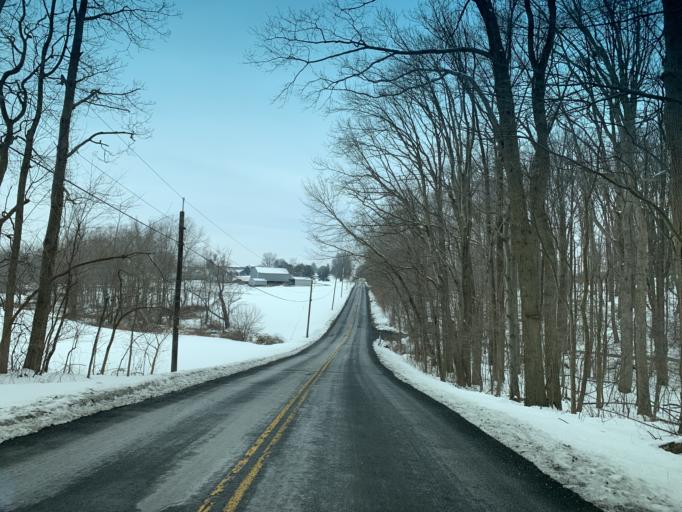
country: US
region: Pennsylvania
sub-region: York County
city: Susquehanna Trails
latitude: 39.7074
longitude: -76.4207
